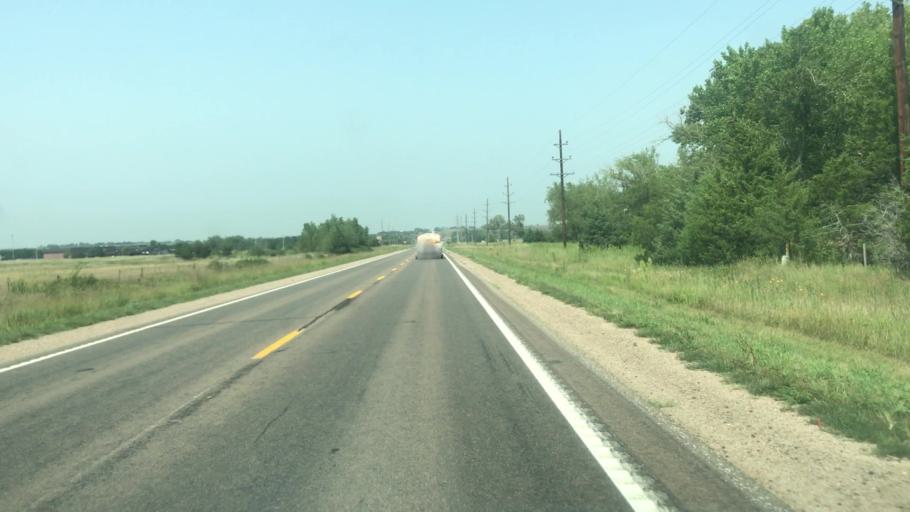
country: US
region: Nebraska
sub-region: Howard County
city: Saint Paul
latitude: 41.0558
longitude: -98.6139
